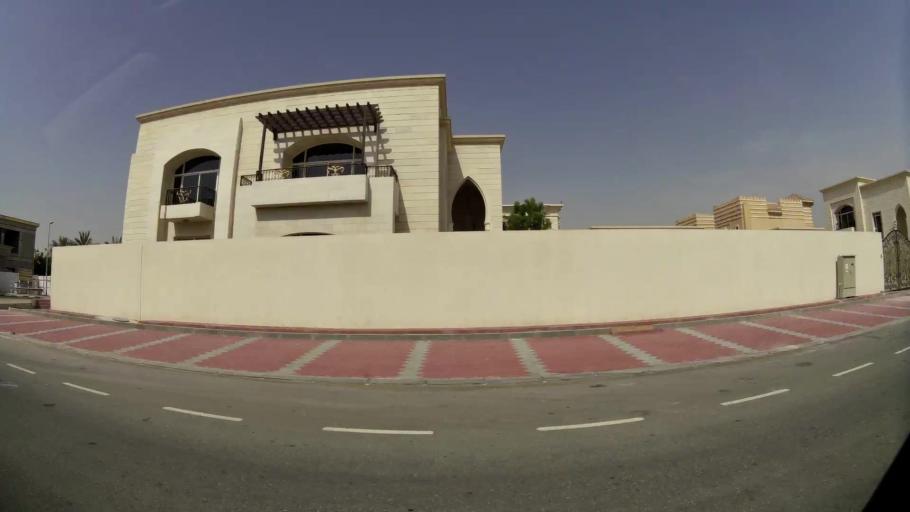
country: AE
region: Ash Shariqah
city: Sharjah
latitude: 25.2497
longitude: 55.4317
